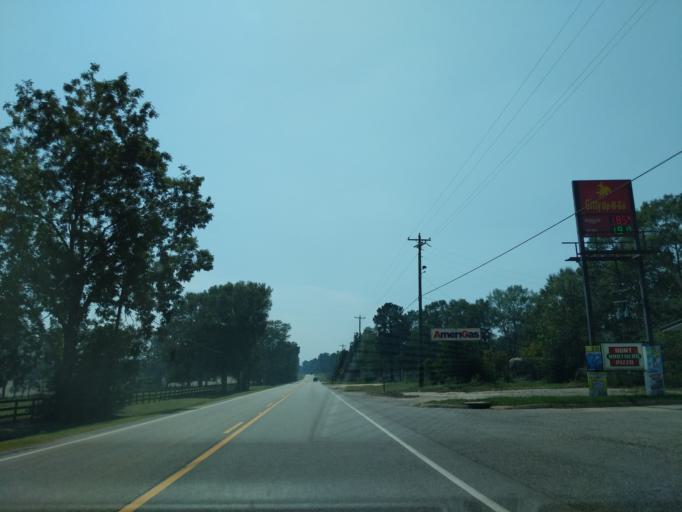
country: US
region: Alabama
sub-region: Covington County
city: Andalusia
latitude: 31.2724
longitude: -86.5092
